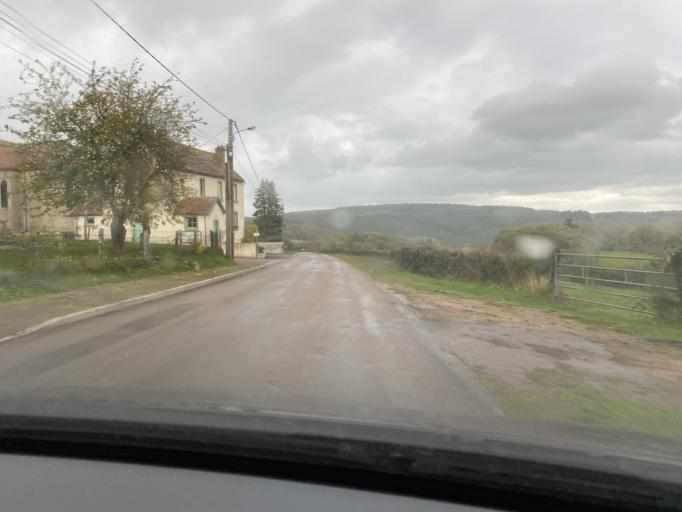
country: FR
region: Bourgogne
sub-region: Departement de la Cote-d'Or
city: Saulieu
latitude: 47.3453
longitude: 4.2135
